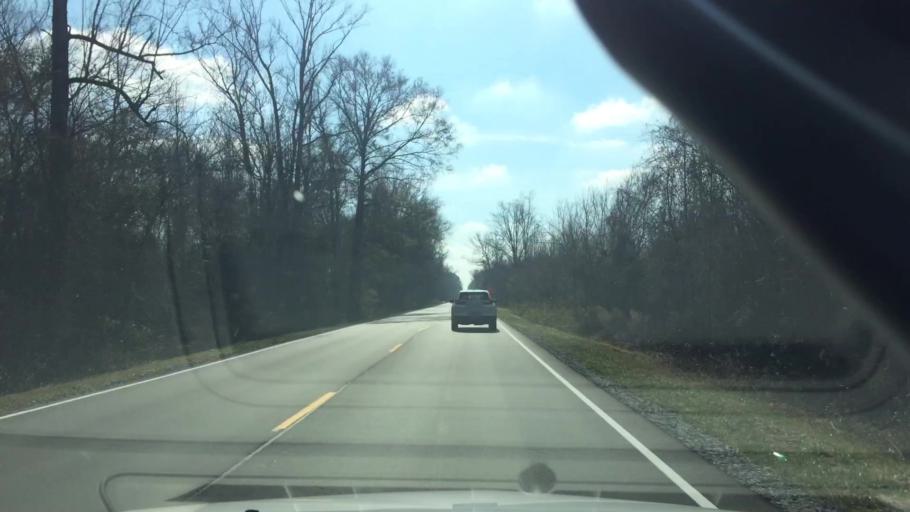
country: US
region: North Carolina
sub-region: Duplin County
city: Beulaville
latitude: 34.9488
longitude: -77.7675
